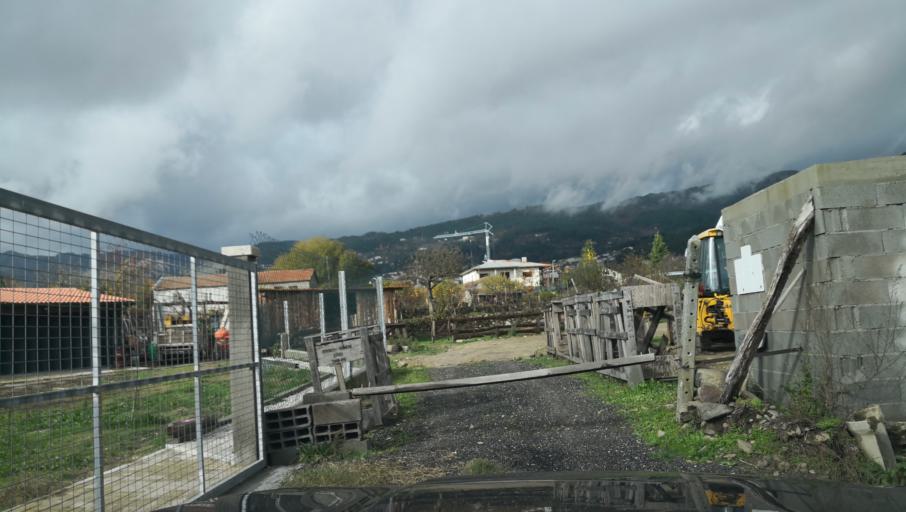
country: PT
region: Vila Real
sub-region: Vila Real
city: Vila Real
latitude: 41.3148
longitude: -7.7576
